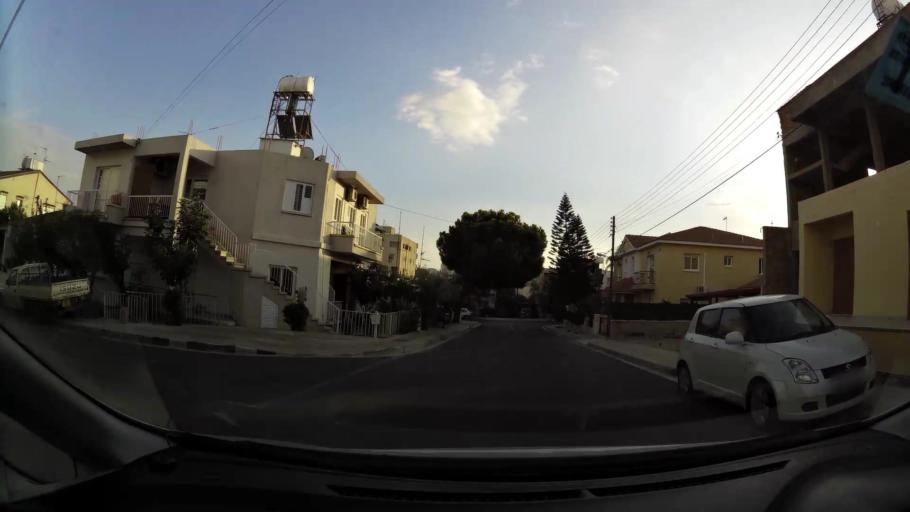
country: CY
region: Lefkosia
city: Nicosia
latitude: 35.1602
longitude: 33.3910
